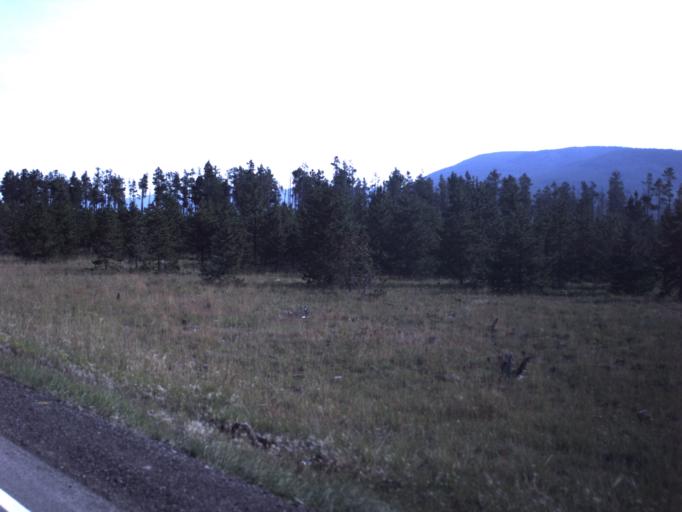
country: US
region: Utah
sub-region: Uintah County
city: Maeser
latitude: 40.7464
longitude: -109.4722
